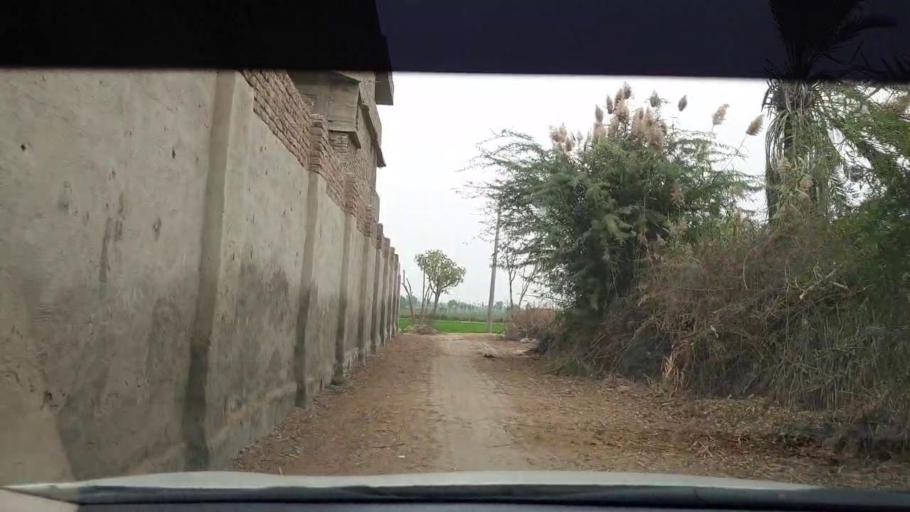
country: PK
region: Sindh
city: Berani
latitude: 25.8568
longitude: 68.8063
